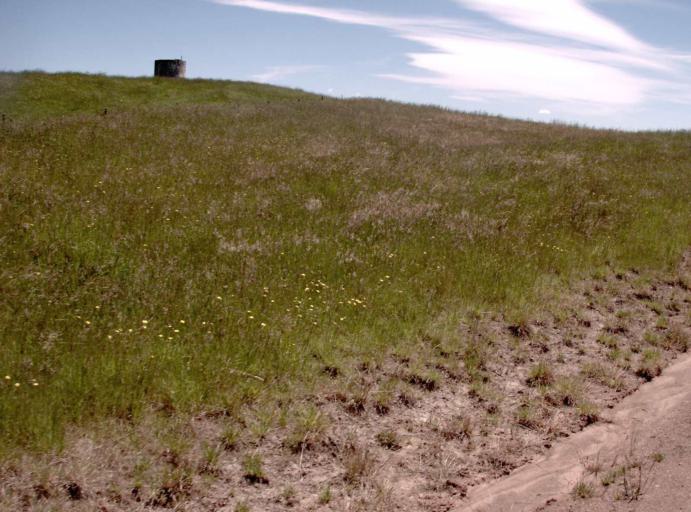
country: AU
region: New South Wales
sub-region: Snowy River
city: Jindabyne
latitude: -37.0926
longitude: 148.2538
